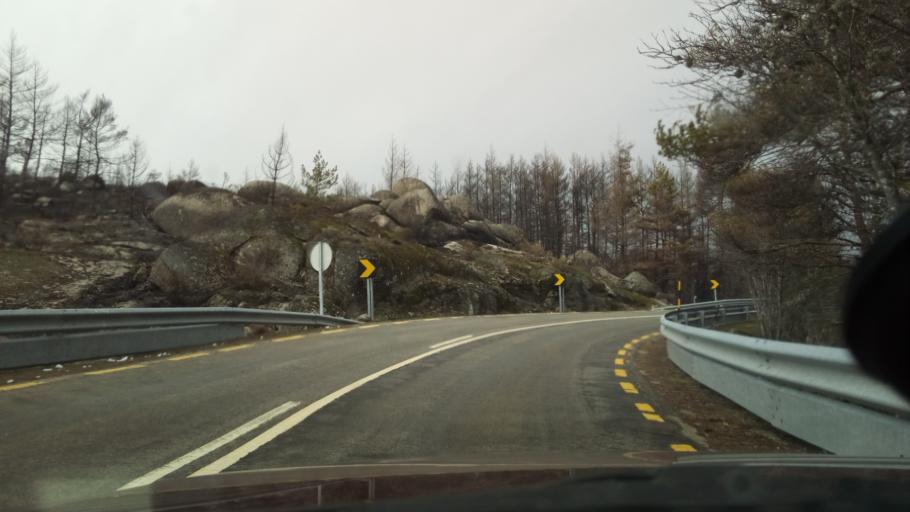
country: PT
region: Guarda
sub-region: Manteigas
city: Manteigas
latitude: 40.4137
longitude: -7.5816
